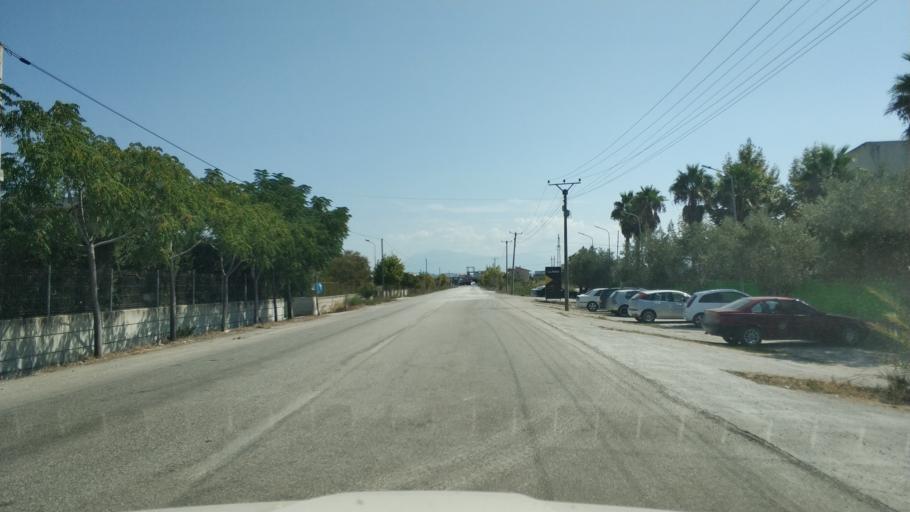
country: AL
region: Fier
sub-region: Rrethi i Lushnjes
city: Krutja e Poshtme
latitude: 40.8805
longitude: 19.6653
